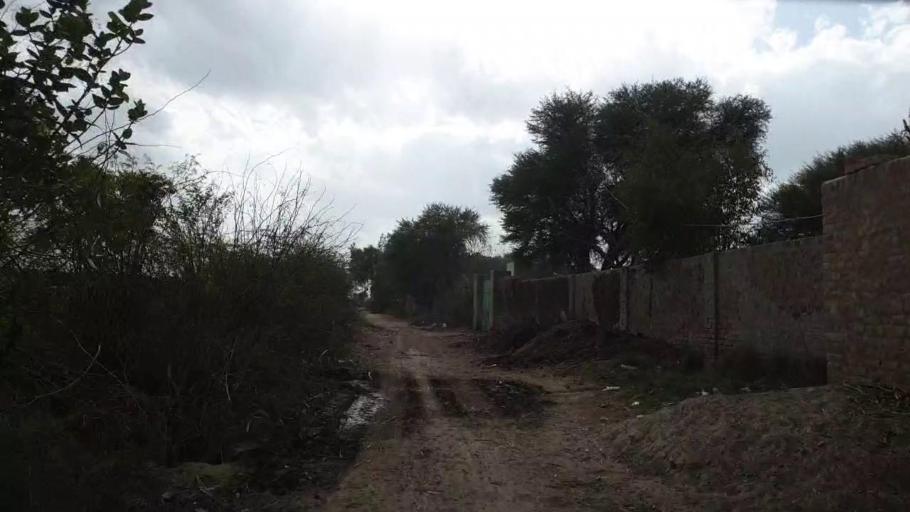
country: PK
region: Sindh
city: Tando Jam
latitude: 25.5436
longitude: 68.5721
